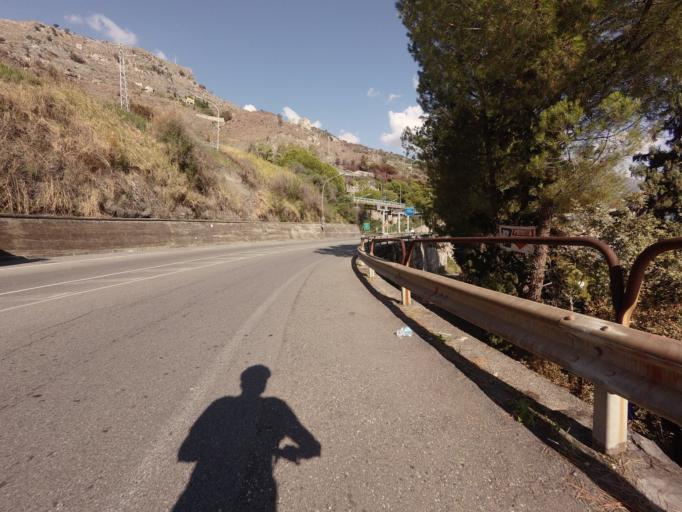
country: IT
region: Sicily
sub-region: Messina
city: Taormina
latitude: 37.8629
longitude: 15.2959
